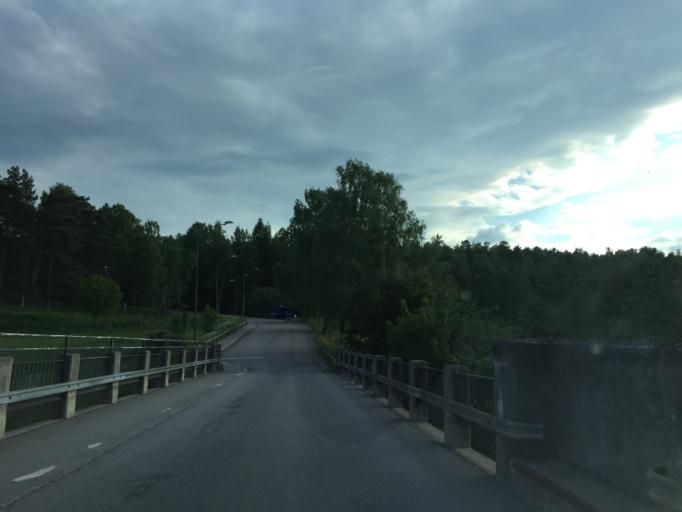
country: SE
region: Vaestmanland
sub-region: Arboga Kommun
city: Arboga
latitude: 59.3914
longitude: 15.8262
